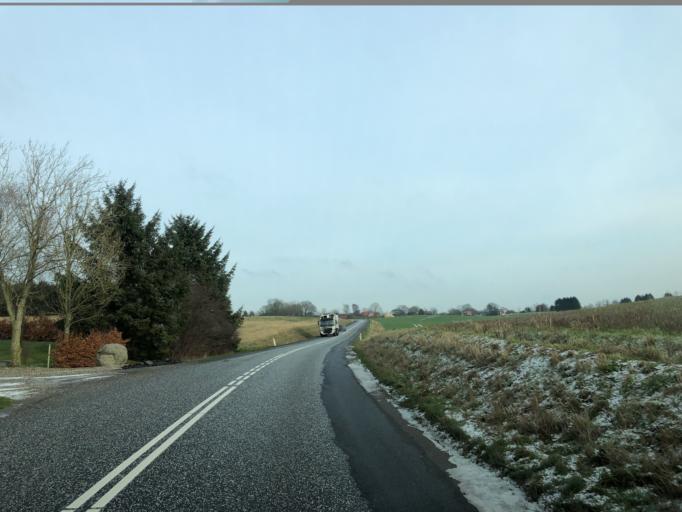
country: DK
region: Central Jutland
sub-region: Hedensted Kommune
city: Torring
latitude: 55.8091
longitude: 9.4650
